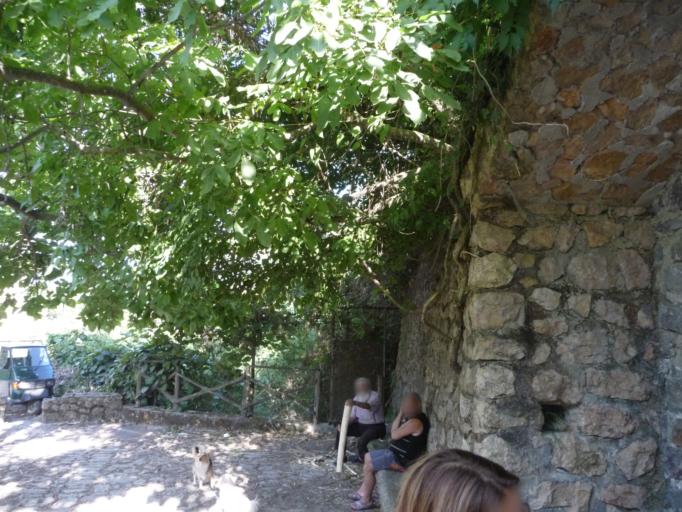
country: IT
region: Calabria
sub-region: Provincia di Reggio Calabria
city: Bivongi
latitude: 38.4833
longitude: 16.4382
